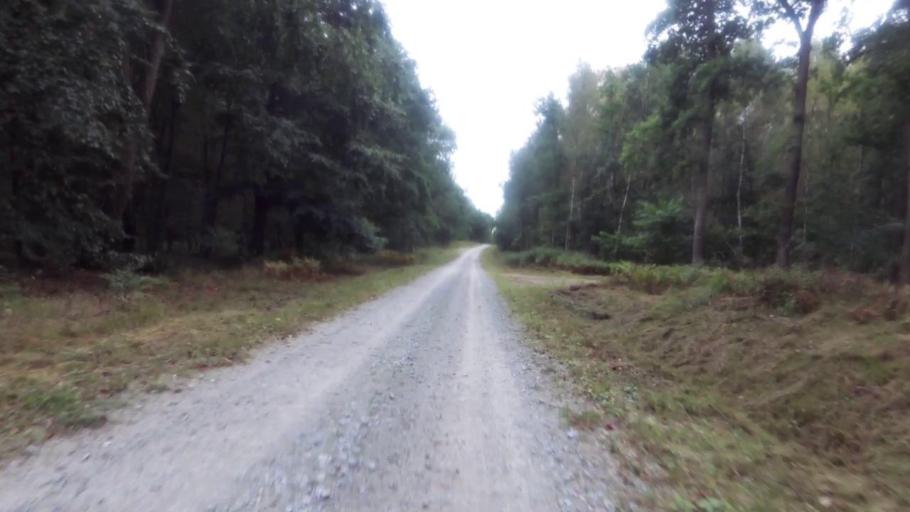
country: PL
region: Lubusz
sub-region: Powiat gorzowski
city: Kostrzyn nad Odra
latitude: 52.6395
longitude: 14.6446
